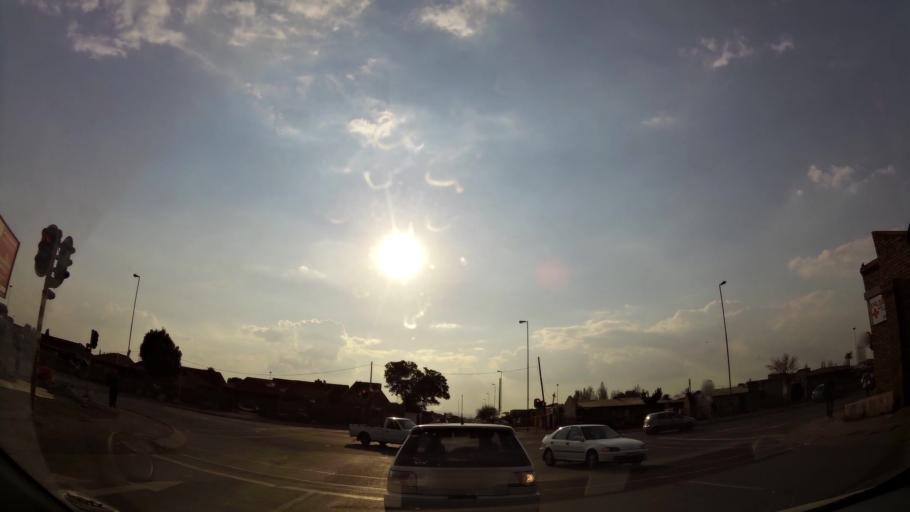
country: ZA
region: Gauteng
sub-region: Ekurhuleni Metropolitan Municipality
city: Germiston
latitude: -26.3579
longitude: 28.1942
